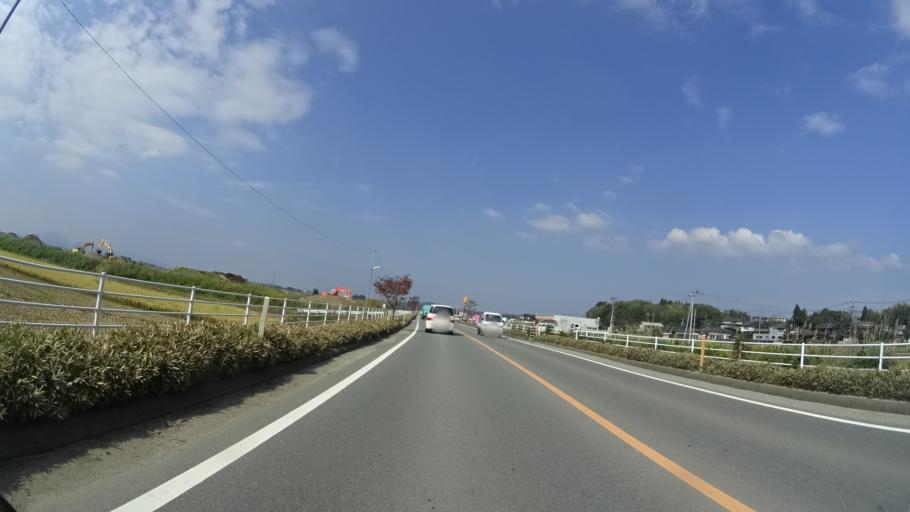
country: JP
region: Kumamoto
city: Ozu
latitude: 32.7718
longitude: 130.8233
